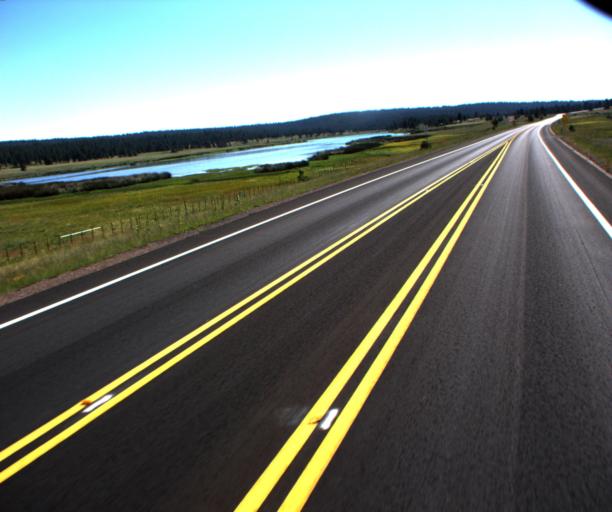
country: US
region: Arizona
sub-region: Apache County
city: Eagar
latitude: 33.8274
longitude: -109.0970
